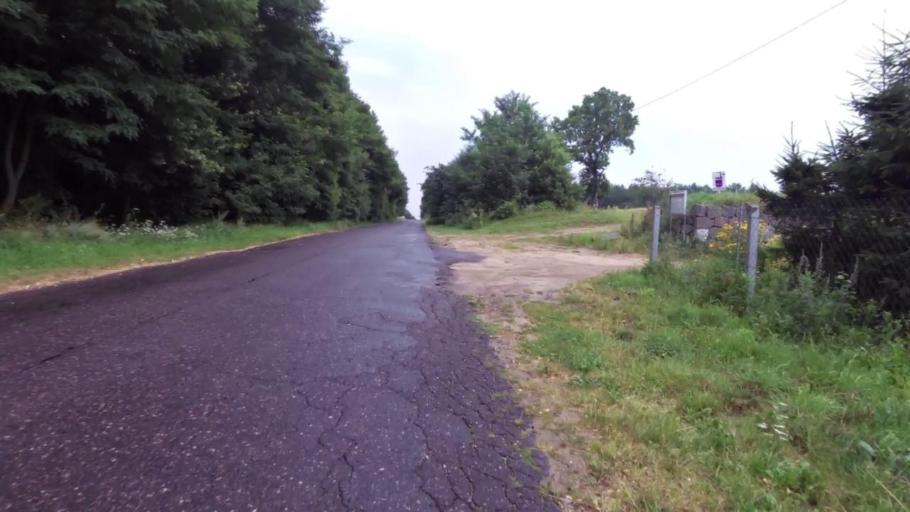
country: PL
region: West Pomeranian Voivodeship
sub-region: Powiat stargardzki
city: Insko
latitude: 53.4777
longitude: 15.6053
